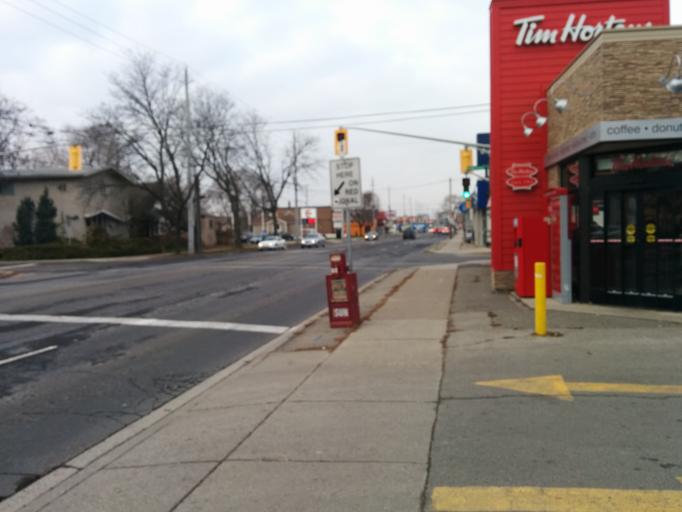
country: CA
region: Ontario
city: Ancaster
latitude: 43.2577
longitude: -79.9253
